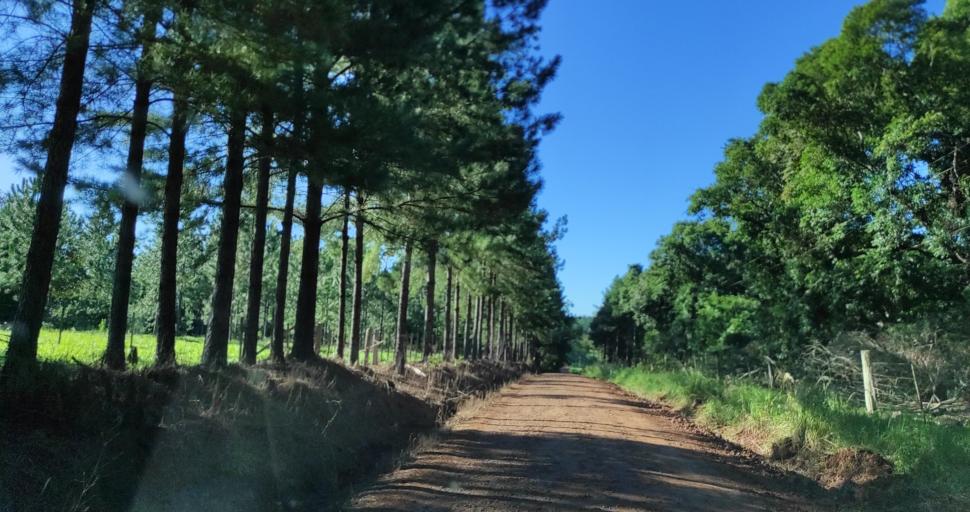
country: AR
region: Misiones
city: Puerto Rico
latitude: -26.8405
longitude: -55.0024
